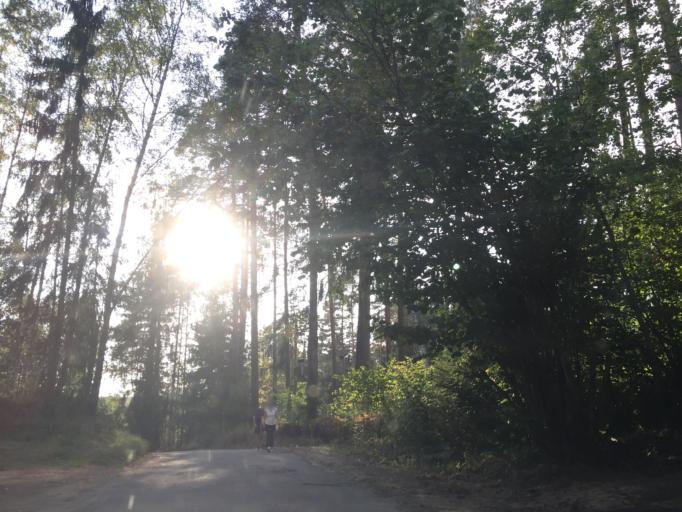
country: LV
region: Baldone
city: Baldone
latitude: 56.7741
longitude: 24.4019
